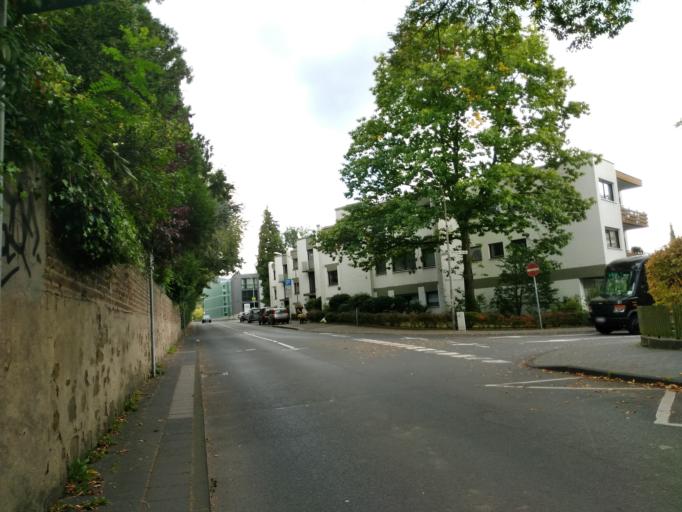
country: DE
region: North Rhine-Westphalia
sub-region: Regierungsbezirk Koln
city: Bad Honnef
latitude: 50.6427
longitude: 7.2315
